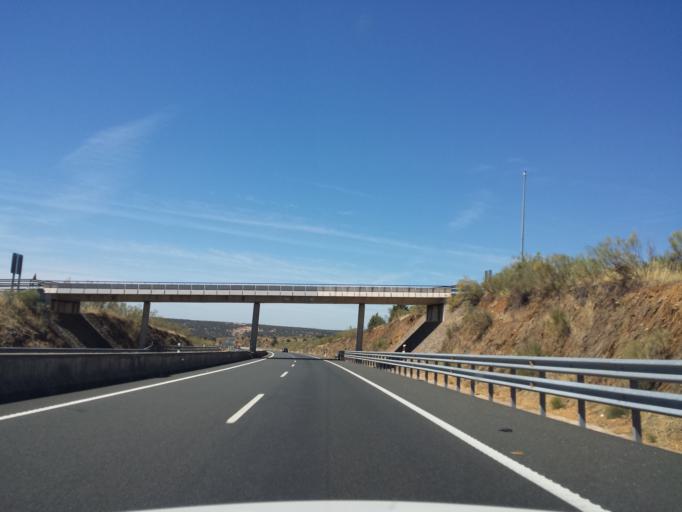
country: ES
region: Extremadura
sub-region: Provincia de Caceres
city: Jaraicejo
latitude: 39.6600
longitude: -5.7943
